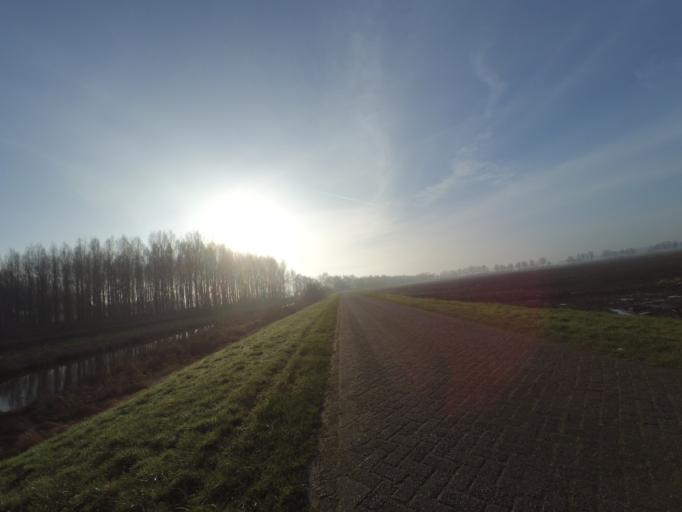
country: NL
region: Drenthe
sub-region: Gemeente Borger-Odoorn
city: Borger
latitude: 52.8940
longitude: 6.7608
